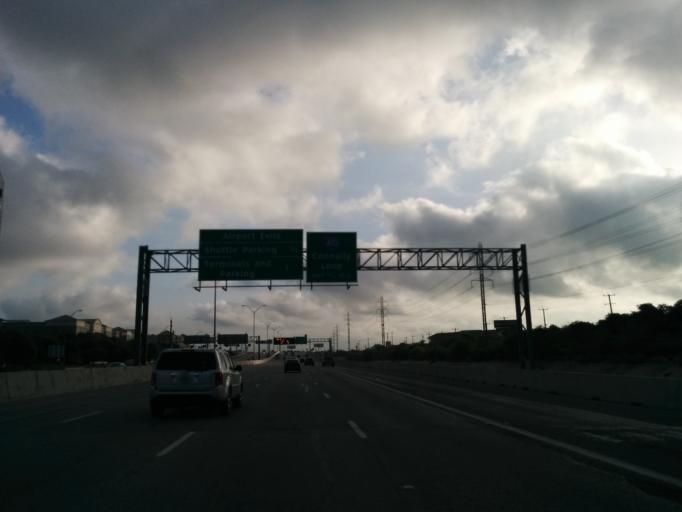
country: US
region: Texas
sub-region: Bexar County
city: Alamo Heights
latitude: 29.5032
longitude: -98.4803
